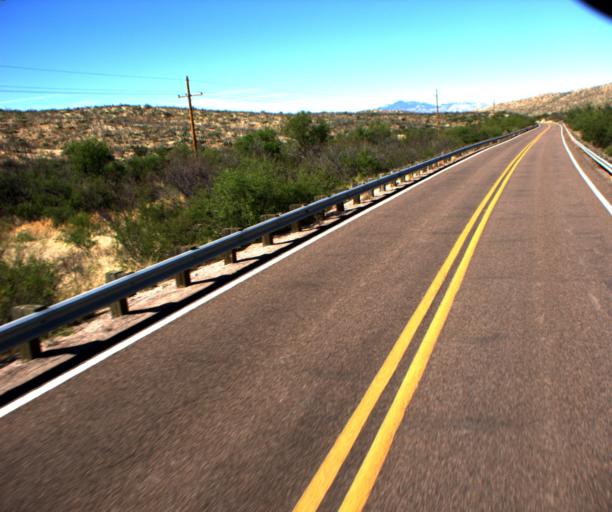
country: US
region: Arizona
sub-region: Pima County
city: Corona de Tucson
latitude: 31.8854
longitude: -110.6726
